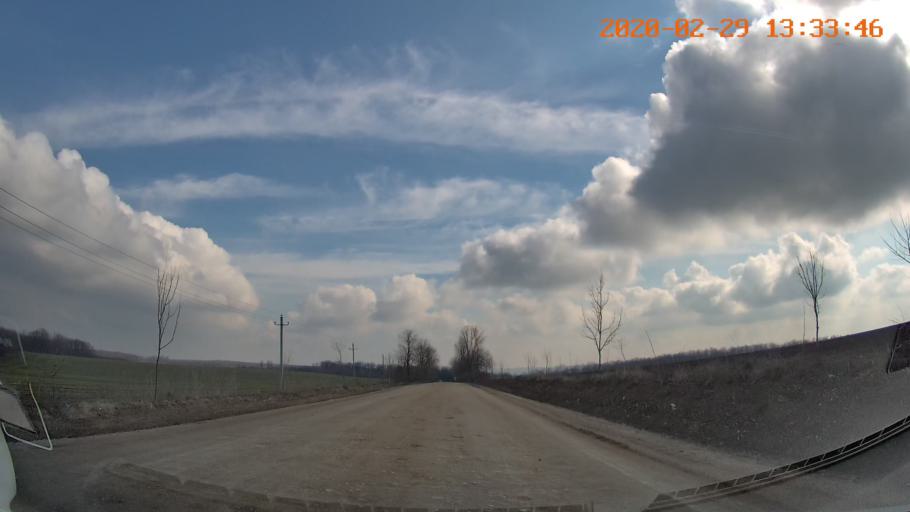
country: MD
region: Telenesti
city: Camenca
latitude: 47.8719
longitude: 28.6186
